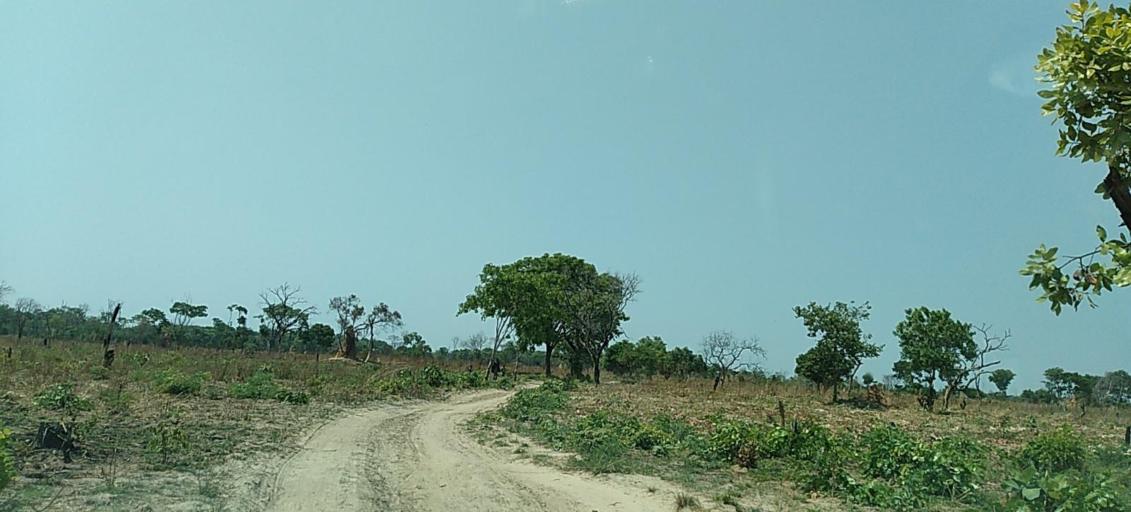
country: ZM
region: Copperbelt
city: Mpongwe
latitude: -13.8591
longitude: 28.0555
